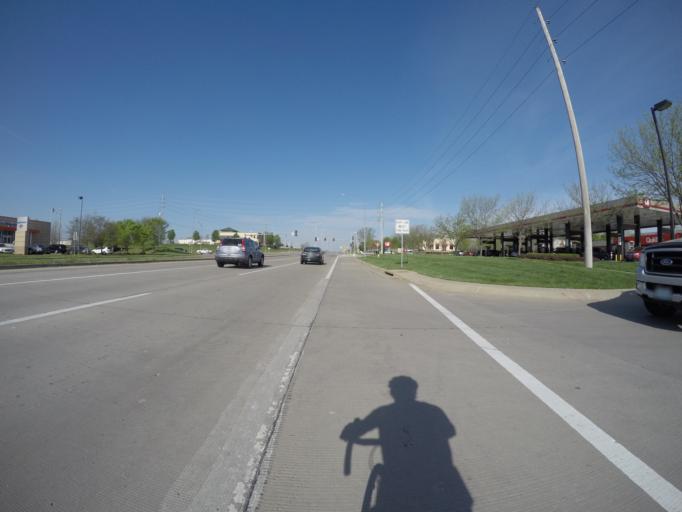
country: US
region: Missouri
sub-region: Cass County
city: Lake Winnebago
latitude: 38.8528
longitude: -94.3782
